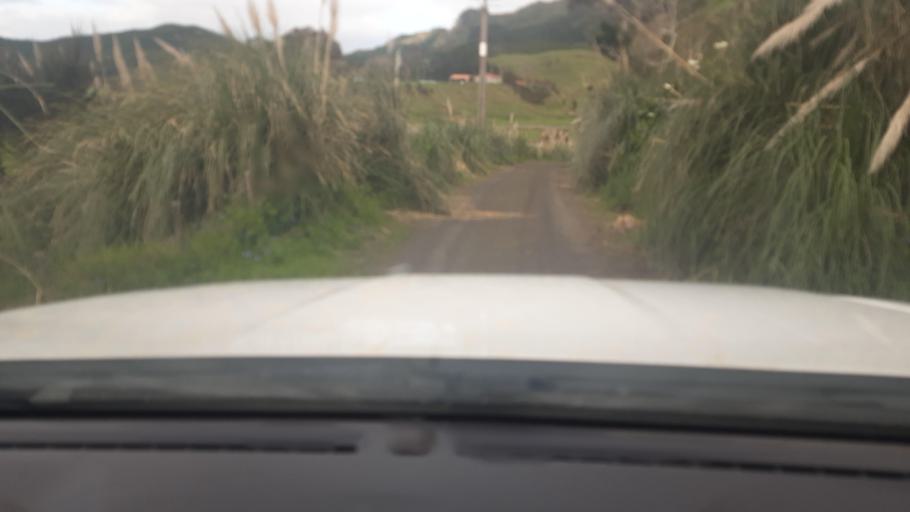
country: NZ
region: Northland
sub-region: Far North District
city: Ahipara
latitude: -35.2602
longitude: 173.1993
